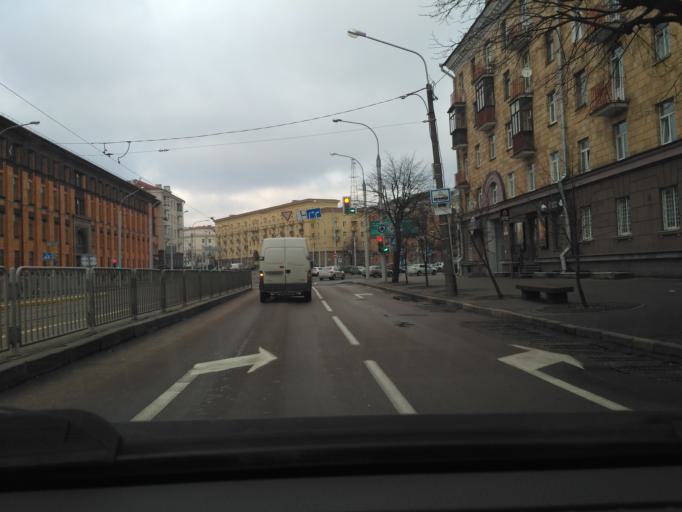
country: BY
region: Minsk
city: Minsk
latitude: 53.9072
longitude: 27.5833
